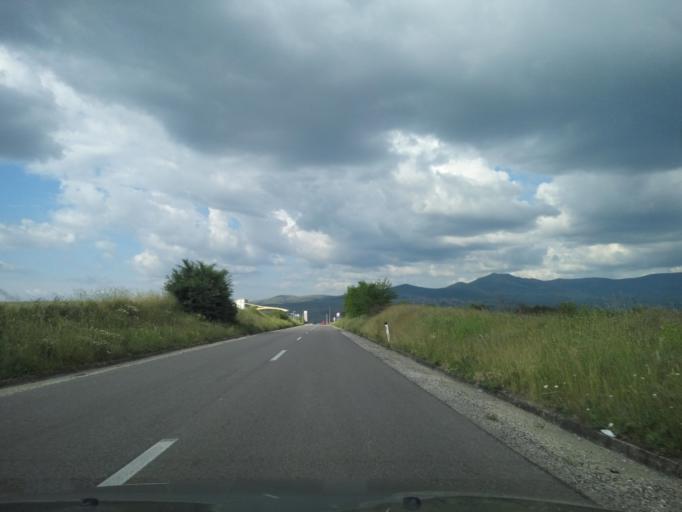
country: XK
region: Gjakova
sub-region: Komuna e Gjakoves
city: Gjakove
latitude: 42.4513
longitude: 20.4988
